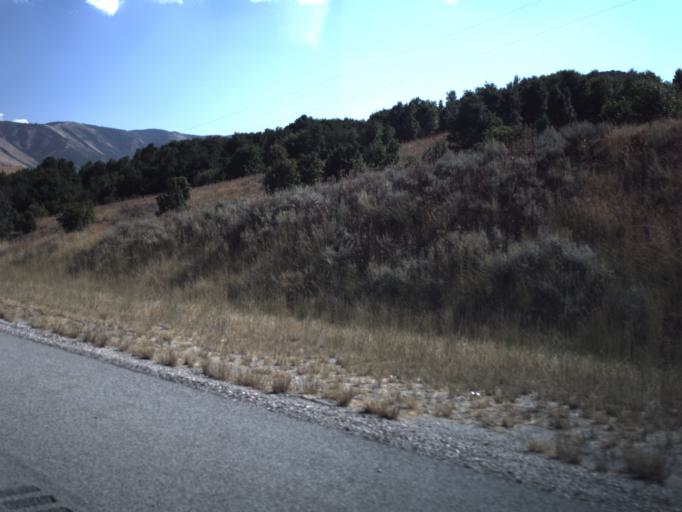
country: US
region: Utah
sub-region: Box Elder County
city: Brigham City
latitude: 41.5295
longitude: -111.9536
